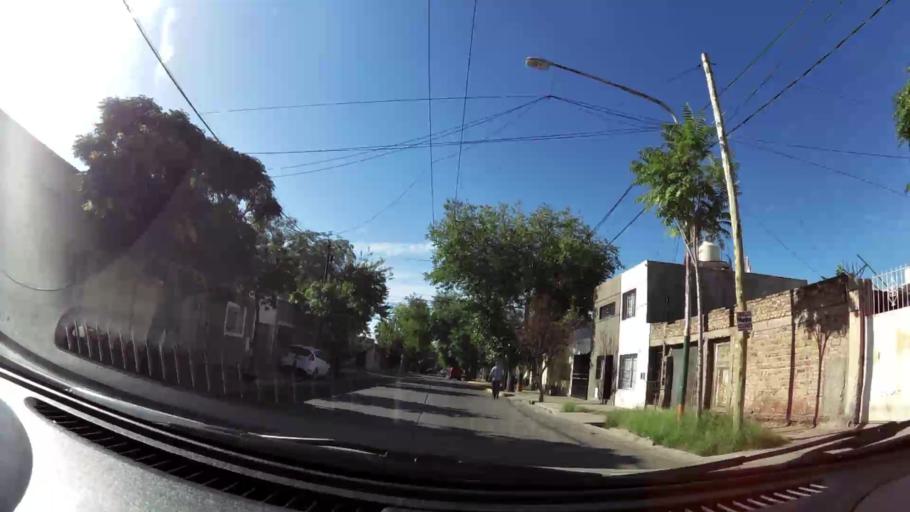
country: AR
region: Mendoza
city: Mendoza
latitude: -32.9013
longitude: -68.8303
